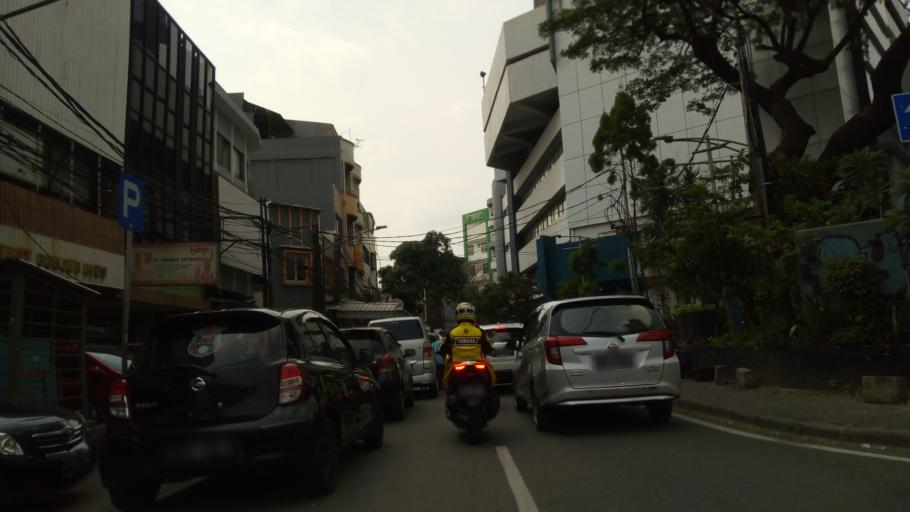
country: ID
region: Jakarta Raya
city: Jakarta
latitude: -6.1614
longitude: 106.8317
